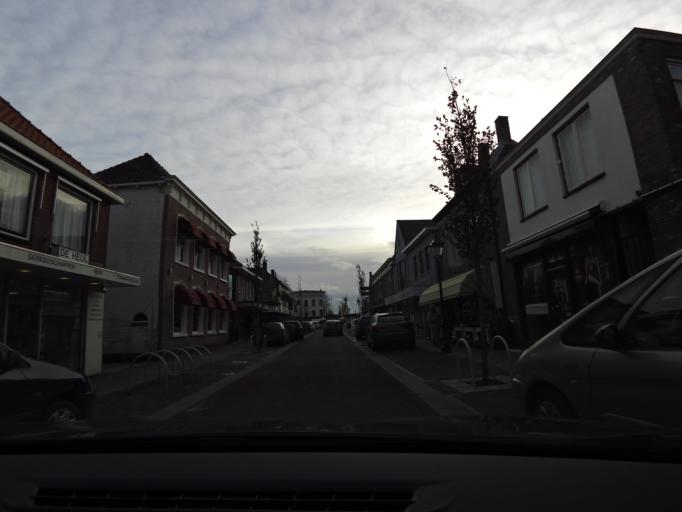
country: NL
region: North Brabant
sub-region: Gemeente Moerdijk
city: Willemstad
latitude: 51.7277
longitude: 4.4380
